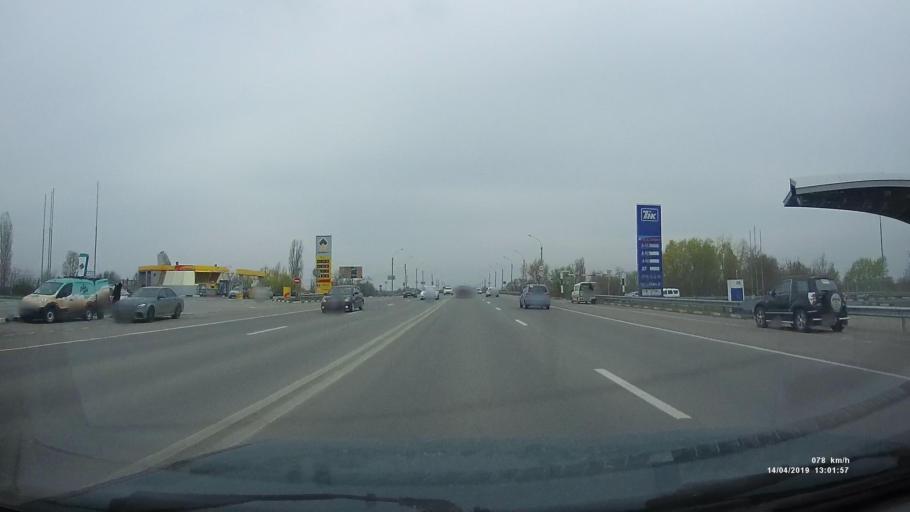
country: RU
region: Rostov
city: Bataysk
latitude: 47.1834
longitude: 39.7381
